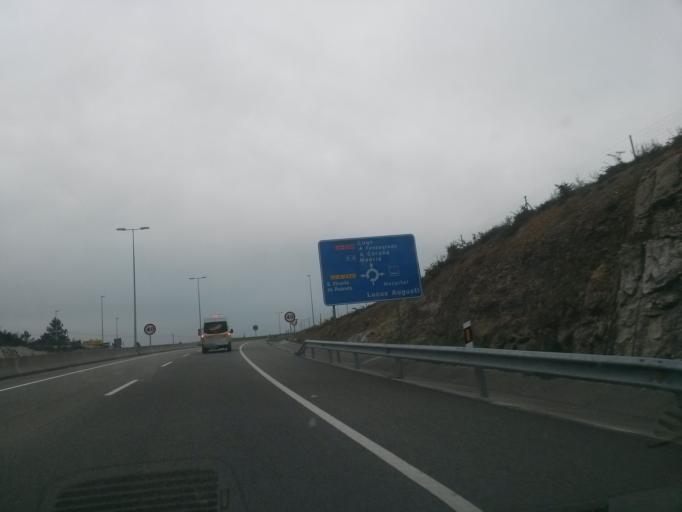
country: ES
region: Galicia
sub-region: Provincia de Lugo
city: Lugo
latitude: 43.0220
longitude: -7.5266
